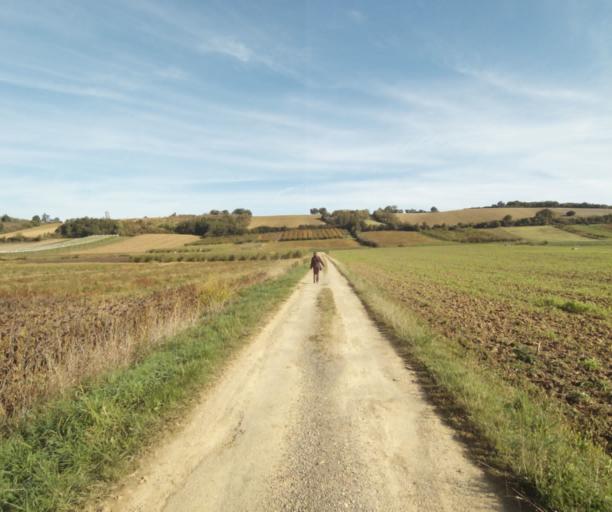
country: FR
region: Midi-Pyrenees
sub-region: Departement du Tarn-et-Garonne
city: Orgueil
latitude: 43.9208
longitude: 1.4344
